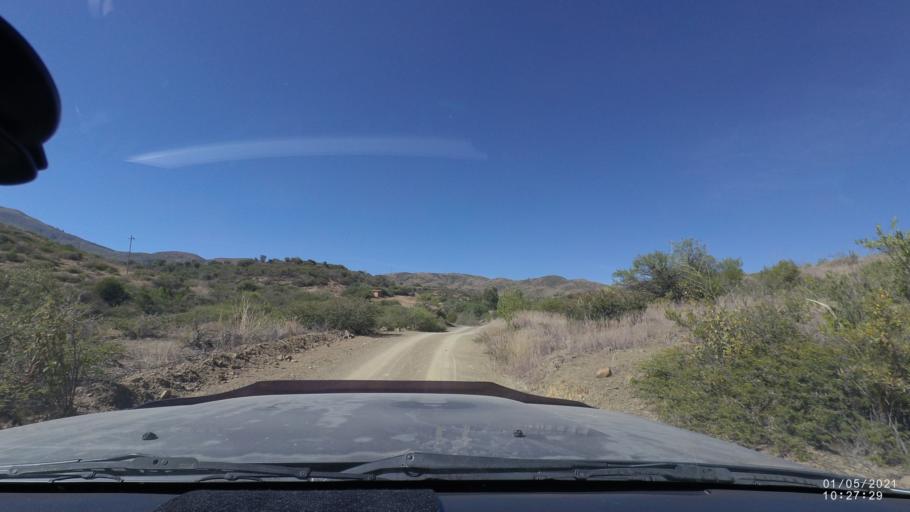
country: BO
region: Cochabamba
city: Capinota
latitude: -17.5852
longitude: -66.1906
